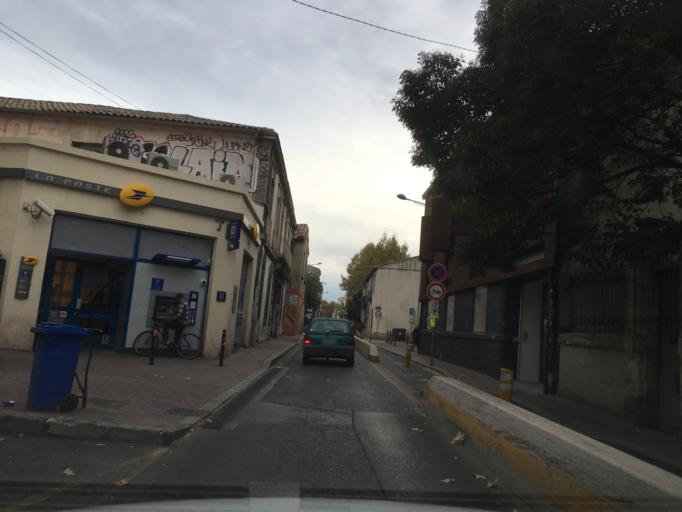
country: FR
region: Languedoc-Roussillon
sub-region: Departement de l'Herault
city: Montpellier
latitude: 43.6113
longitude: 3.8666
